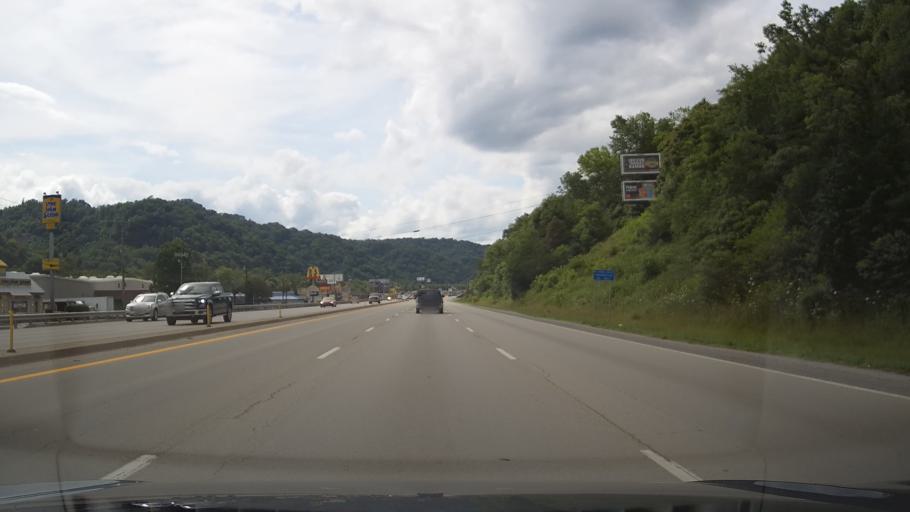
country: US
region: Kentucky
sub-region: Pike County
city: Coal Run Village
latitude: 37.5169
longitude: -82.5623
